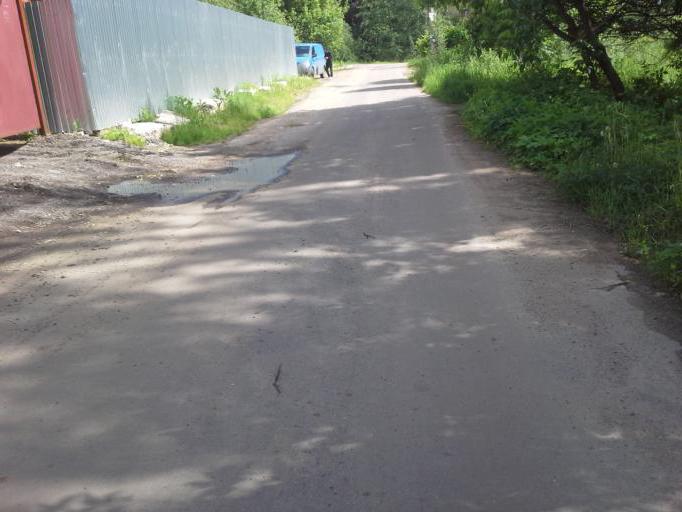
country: RU
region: Moscow
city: Tolstopal'tsevo
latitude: 55.6225
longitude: 37.2154
